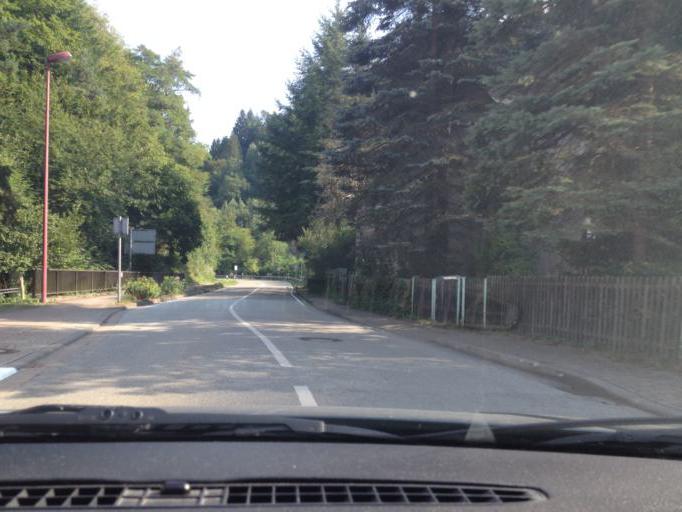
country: DE
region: Rheinland-Pfalz
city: Frankenstein
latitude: 49.4375
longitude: 7.9798
